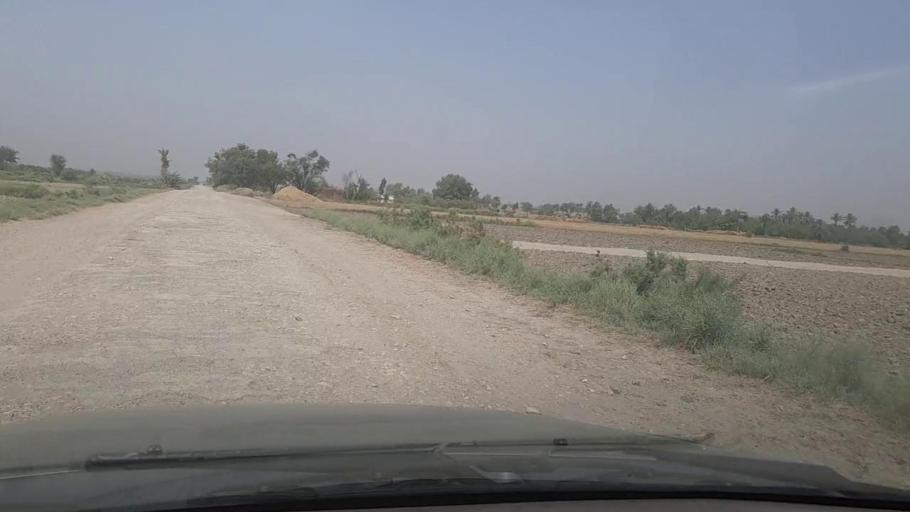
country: PK
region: Sindh
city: Madeji
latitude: 27.7967
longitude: 68.4516
